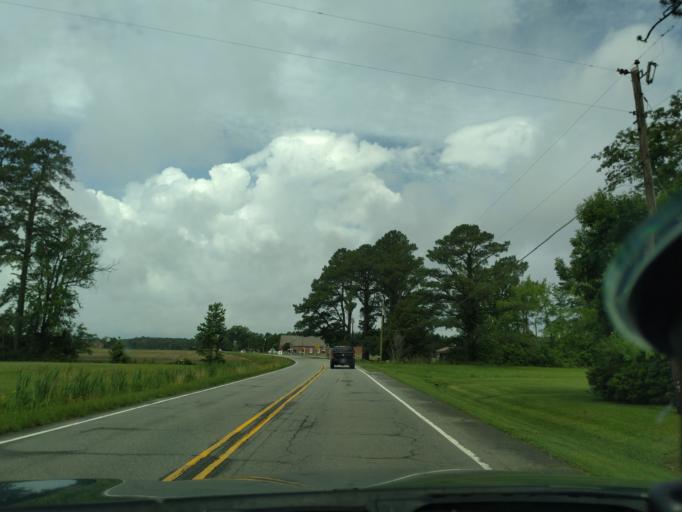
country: US
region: North Carolina
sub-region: Washington County
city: Plymouth
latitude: 35.8760
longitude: -76.6390
